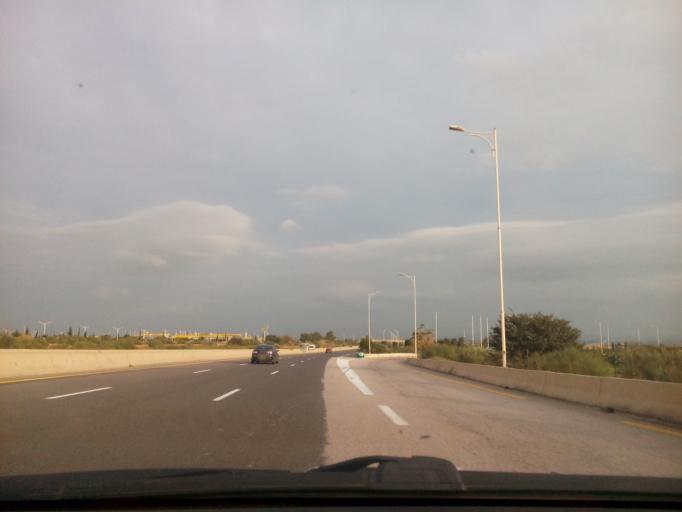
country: DZ
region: Relizane
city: Relizane
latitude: 35.7902
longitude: 0.4020
